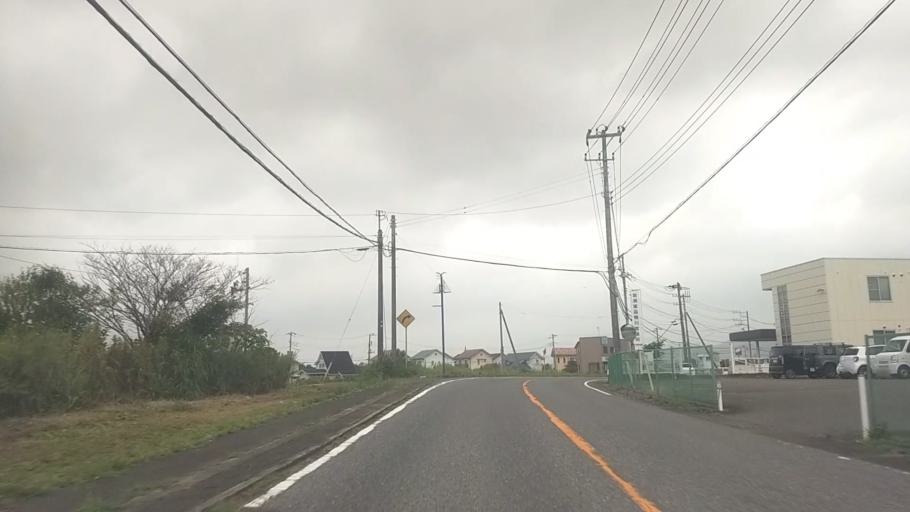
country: JP
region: Chiba
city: Kawaguchi
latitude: 35.1190
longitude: 140.0721
